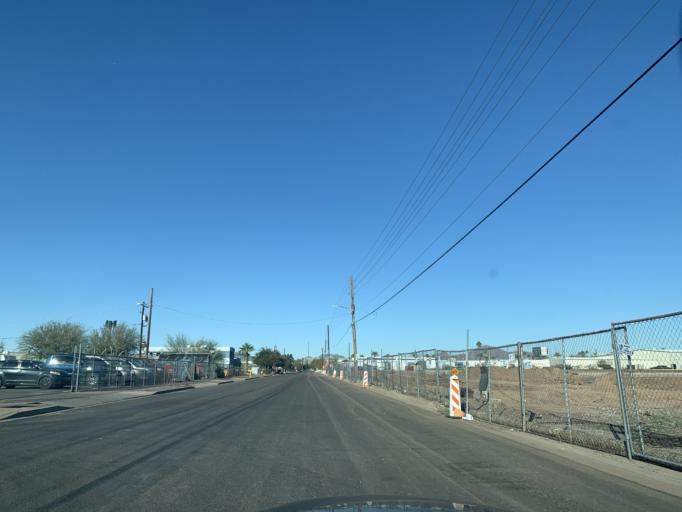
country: US
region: Arizona
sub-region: Maricopa County
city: Tempe Junction
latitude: 33.4188
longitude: -111.9997
